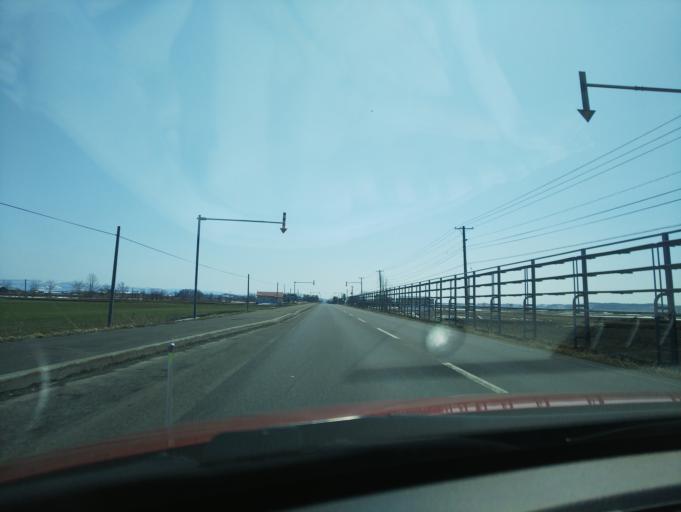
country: JP
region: Hokkaido
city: Nayoro
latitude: 44.2303
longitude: 142.3948
